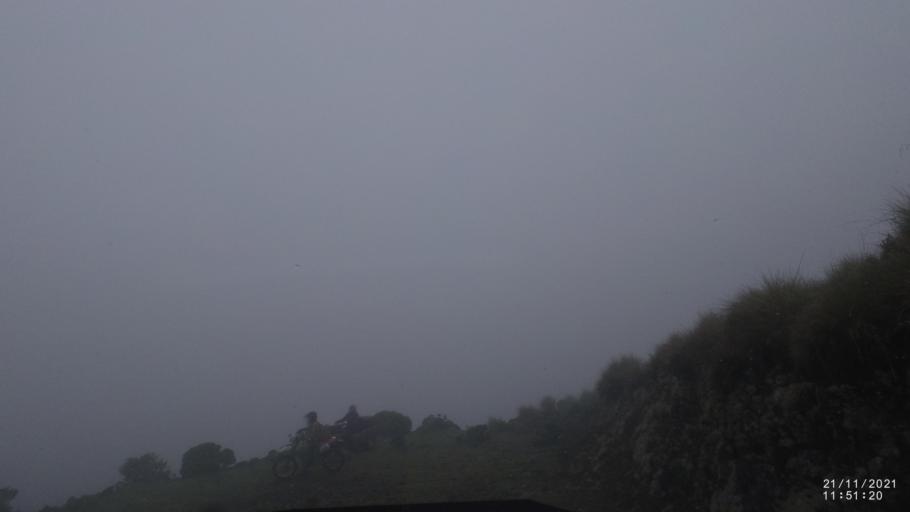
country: BO
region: Cochabamba
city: Cochabamba
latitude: -16.9464
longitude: -66.2554
